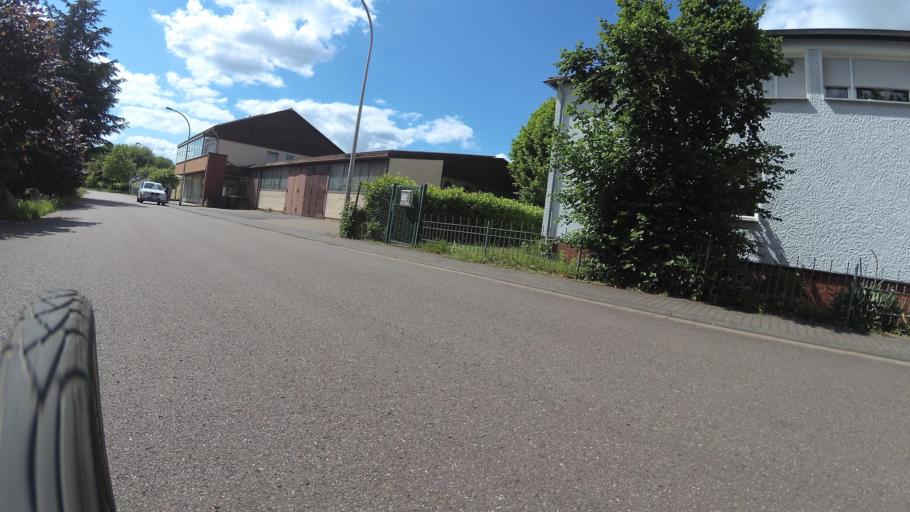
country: DE
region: Saarland
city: Volklingen
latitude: 49.2600
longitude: 6.8619
